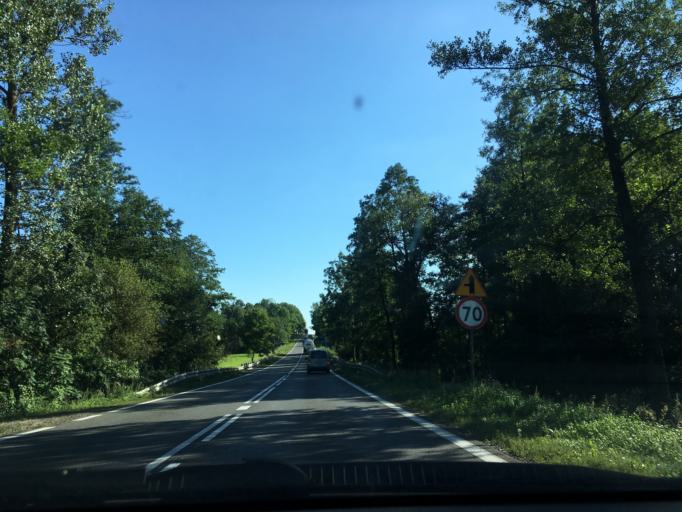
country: PL
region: Podlasie
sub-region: Powiat sokolski
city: Janow
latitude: 53.3957
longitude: 23.1146
